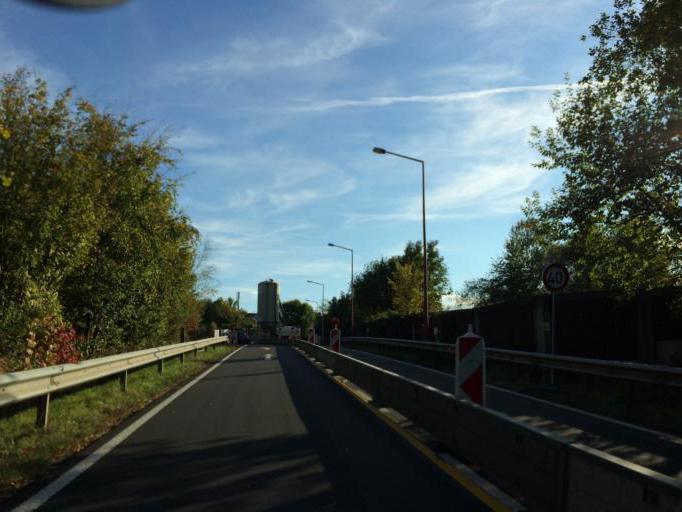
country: DE
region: North Rhine-Westphalia
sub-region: Regierungsbezirk Koln
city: Konigswinter
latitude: 50.7066
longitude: 7.1778
